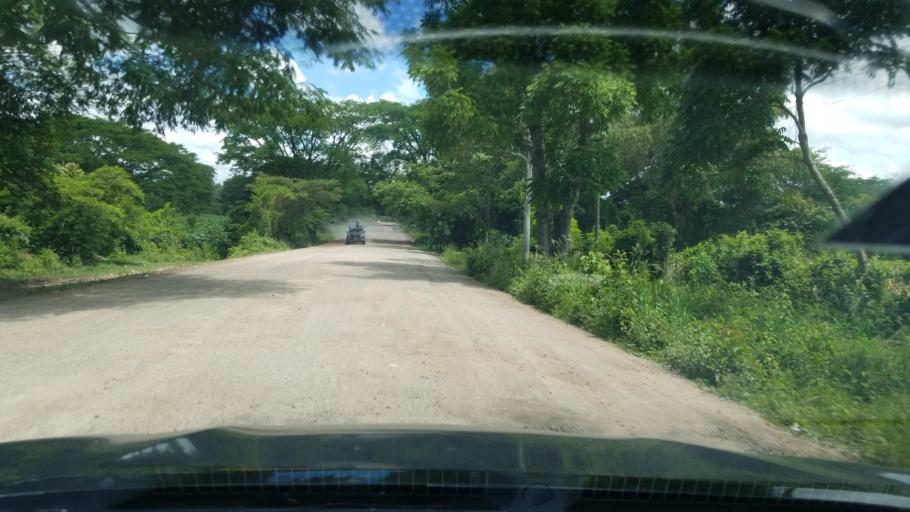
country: HN
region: Francisco Morazan
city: Talanga
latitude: 14.3709
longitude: -87.0569
